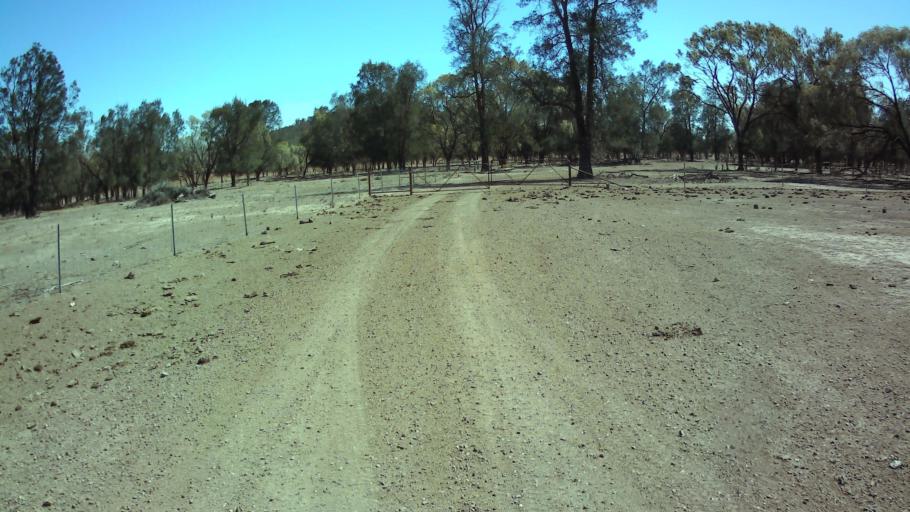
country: AU
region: New South Wales
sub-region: Bland
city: West Wyalong
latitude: -33.7397
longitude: 147.6620
